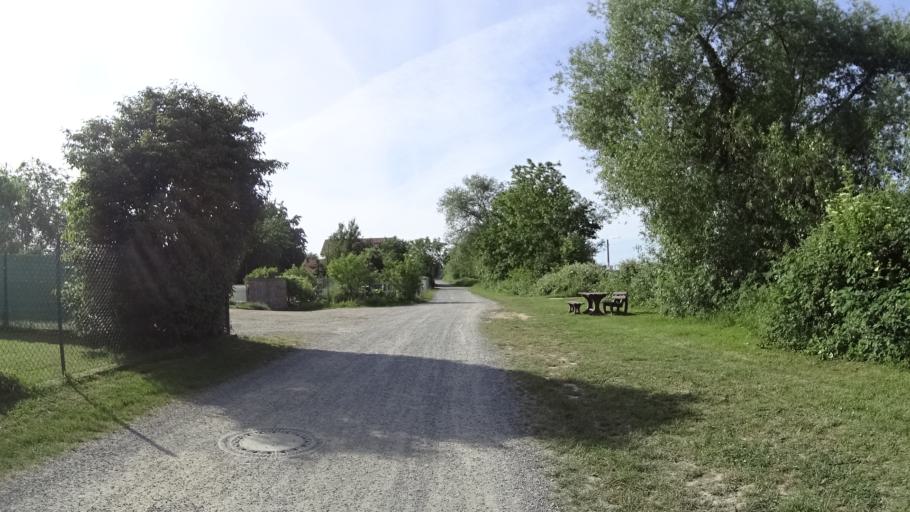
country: DE
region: Bavaria
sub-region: Regierungsbezirk Unterfranken
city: Kleinostheim
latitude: 49.9974
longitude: 9.0623
